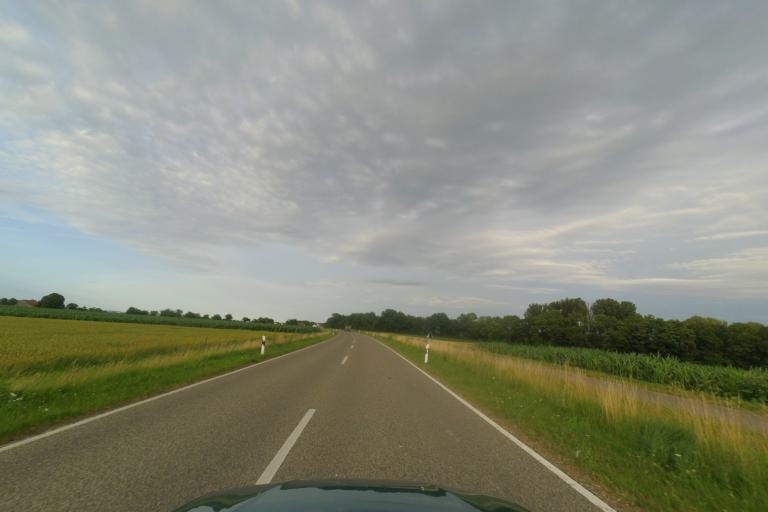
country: DE
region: Bavaria
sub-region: Swabia
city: Hochstadt an der Donau
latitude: 48.6210
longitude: 10.5820
